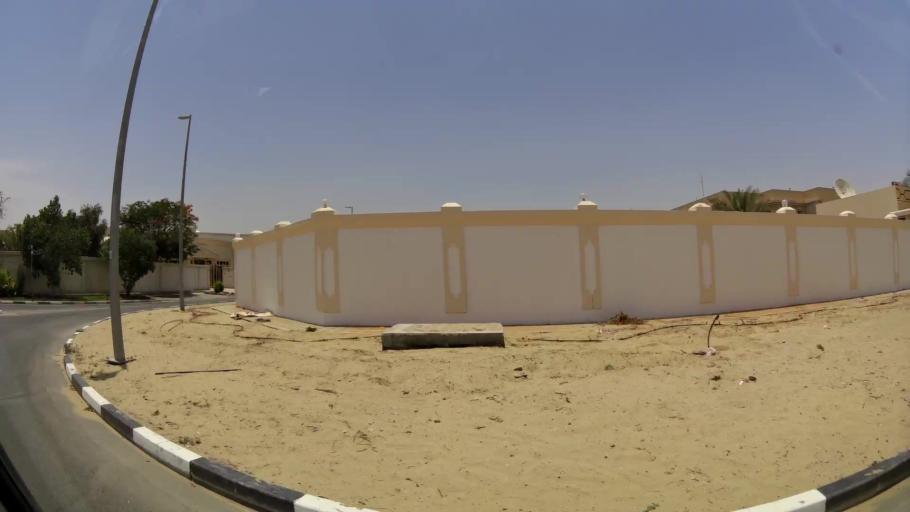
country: AE
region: Ash Shariqah
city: Sharjah
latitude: 25.2323
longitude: 55.4582
